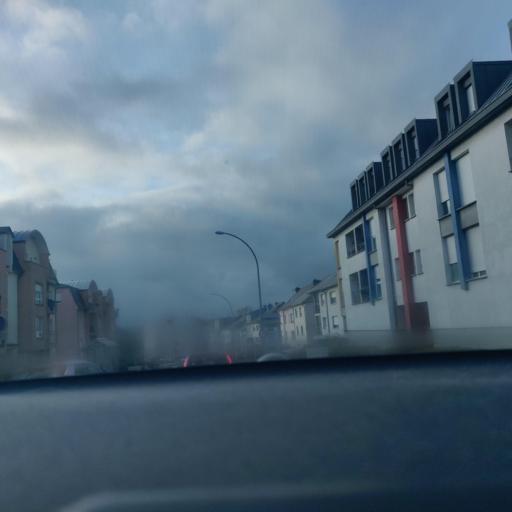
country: LU
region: Luxembourg
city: Soleuvre
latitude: 49.5234
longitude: 5.9324
